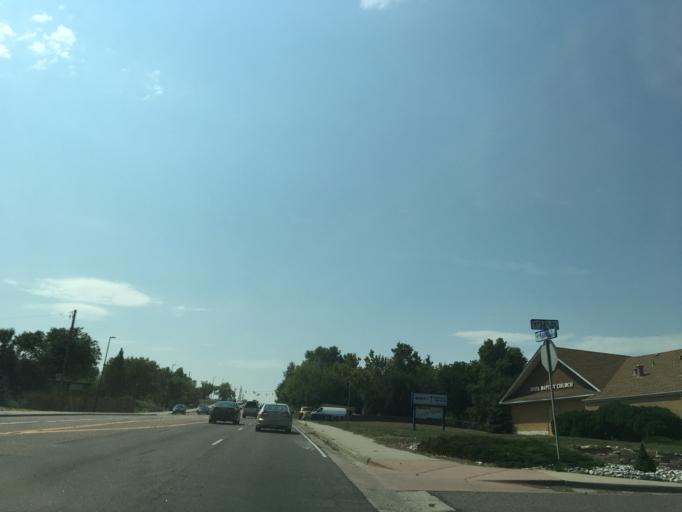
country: US
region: Colorado
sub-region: Jefferson County
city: Wheat Ridge
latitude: 39.7651
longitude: -105.1098
